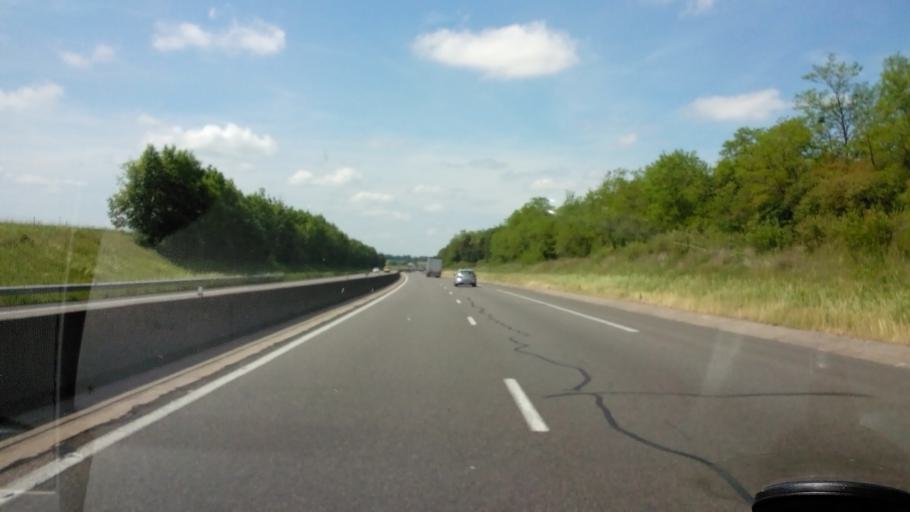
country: FR
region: Lorraine
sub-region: Departement des Vosges
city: Bulgneville
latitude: 48.2142
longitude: 5.8221
